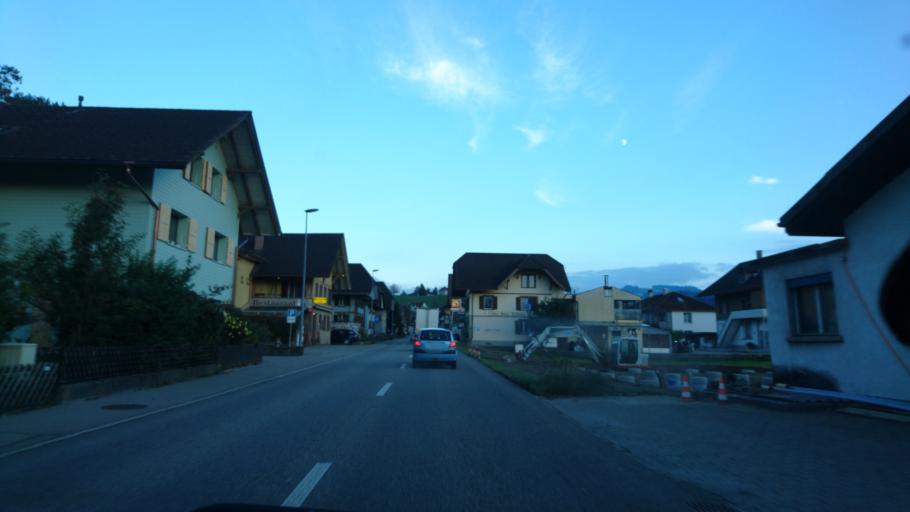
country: CH
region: Bern
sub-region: Emmental District
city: Langnau
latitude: 46.9352
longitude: 7.8064
